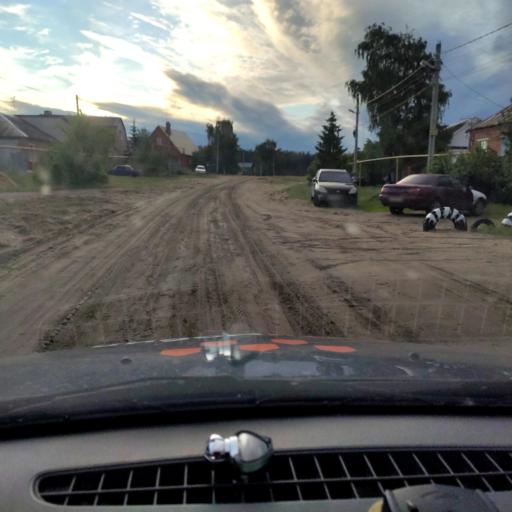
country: RU
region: Voronezj
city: Somovo
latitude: 51.7533
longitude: 39.3244
